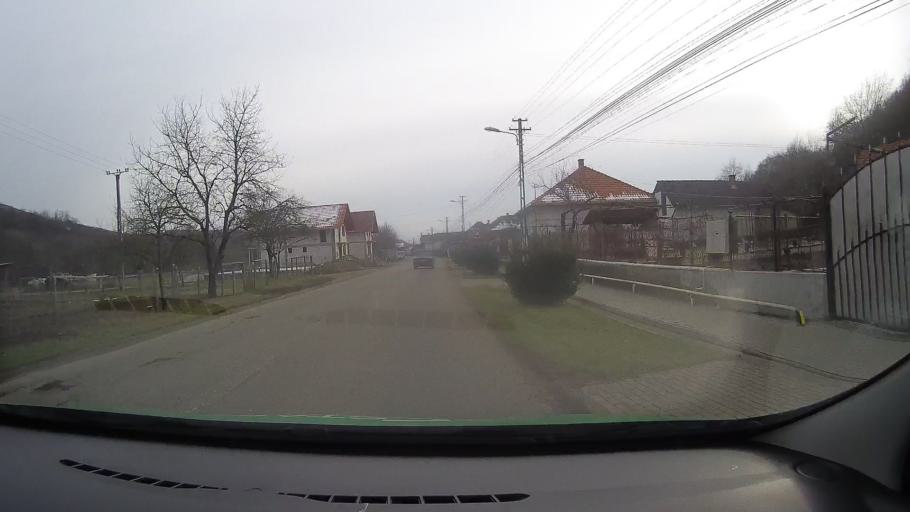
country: RO
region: Hunedoara
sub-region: Comuna Geoagiu
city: Geoagiu
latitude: 45.9336
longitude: 23.1934
